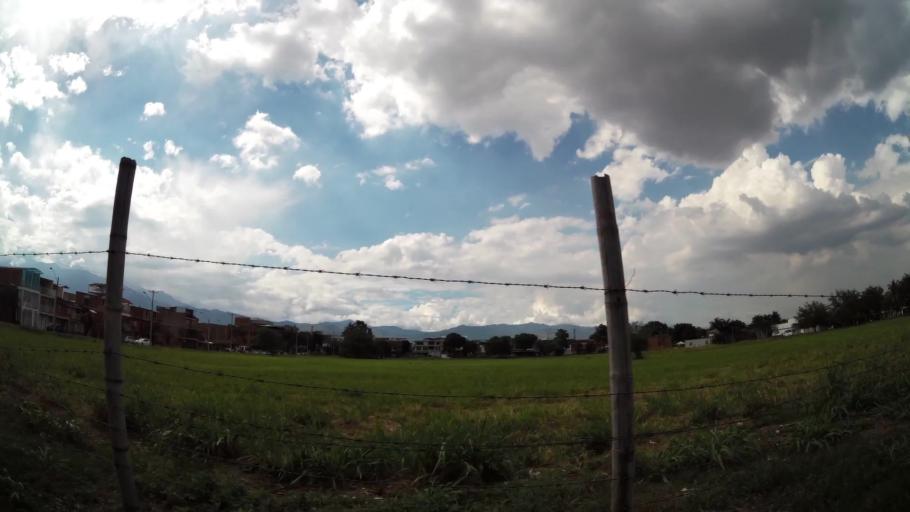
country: CO
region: Valle del Cauca
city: Cali
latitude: 3.3963
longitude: -76.5074
